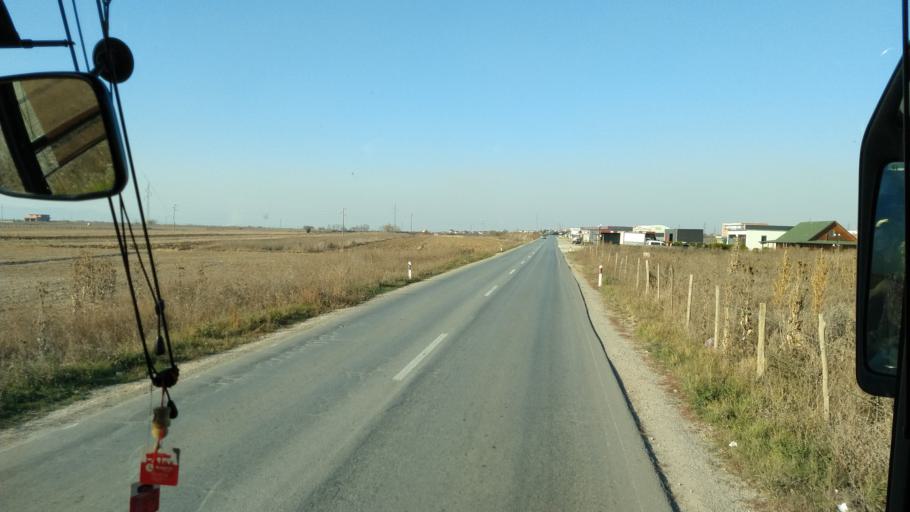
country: XK
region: Pristina
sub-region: Lipjan
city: Lipljan
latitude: 42.5214
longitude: 21.1121
